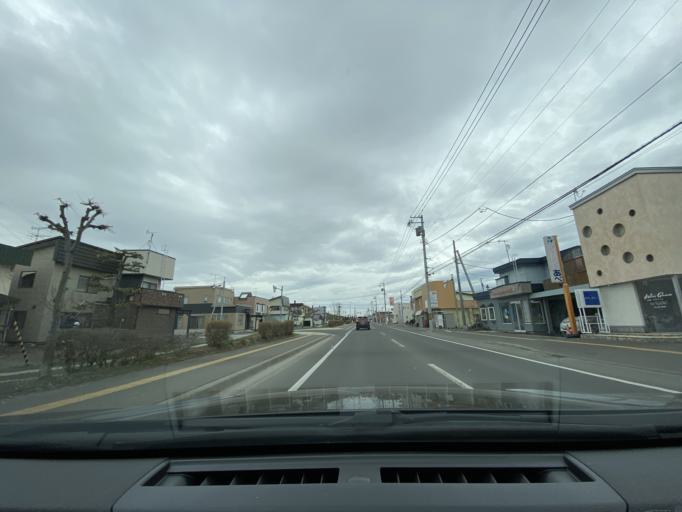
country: JP
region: Hokkaido
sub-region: Asahikawa-shi
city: Asahikawa
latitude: 43.7920
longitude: 142.4160
